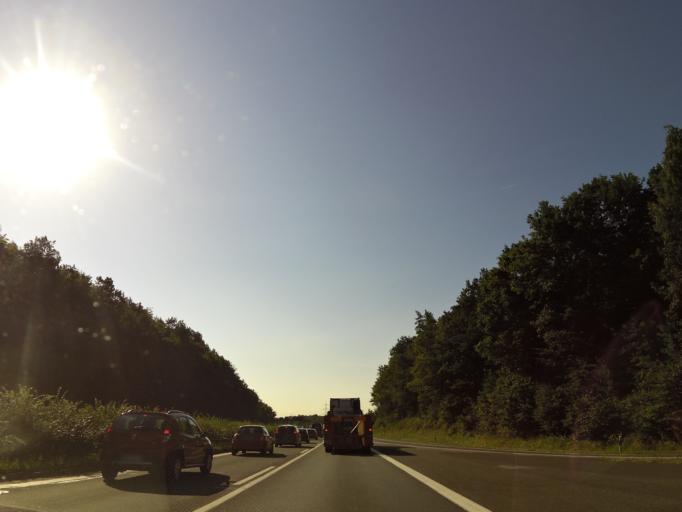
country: DE
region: Bavaria
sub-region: Regierungsbezirk Mittelfranken
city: Obermichelbach
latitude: 49.5658
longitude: 10.9447
